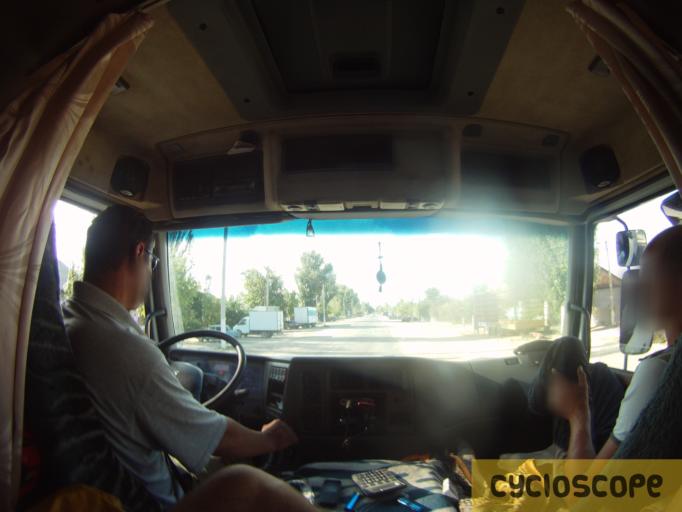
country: KZ
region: Almaty Oblysy
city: Zharkent
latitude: 44.1747
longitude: 80.0190
